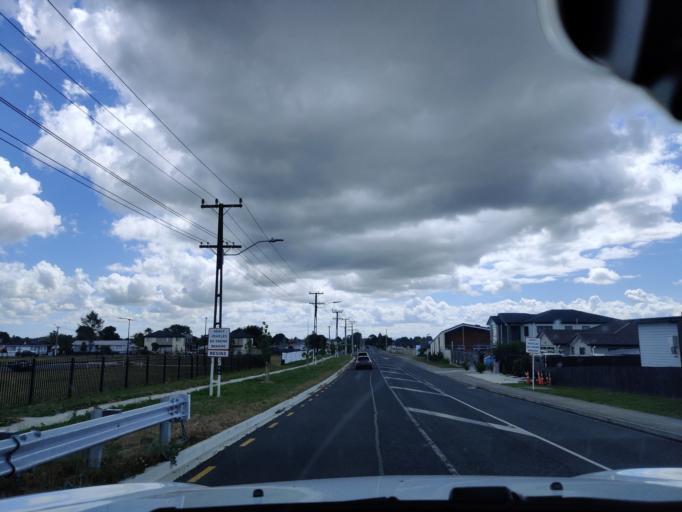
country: NZ
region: Auckland
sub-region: Auckland
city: Red Hill
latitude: -37.0533
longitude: 174.9679
